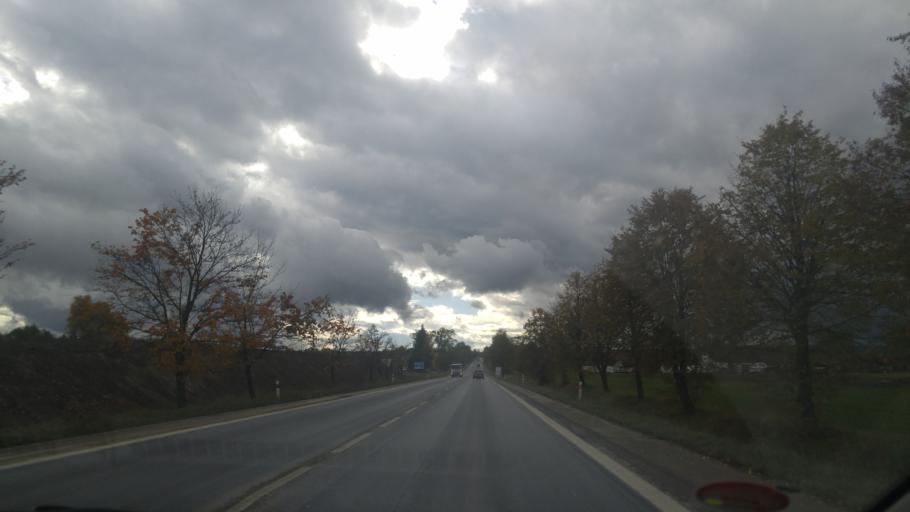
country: CZ
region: Jihocesky
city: Dolni Bukovsko
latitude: 49.1328
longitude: 14.6109
